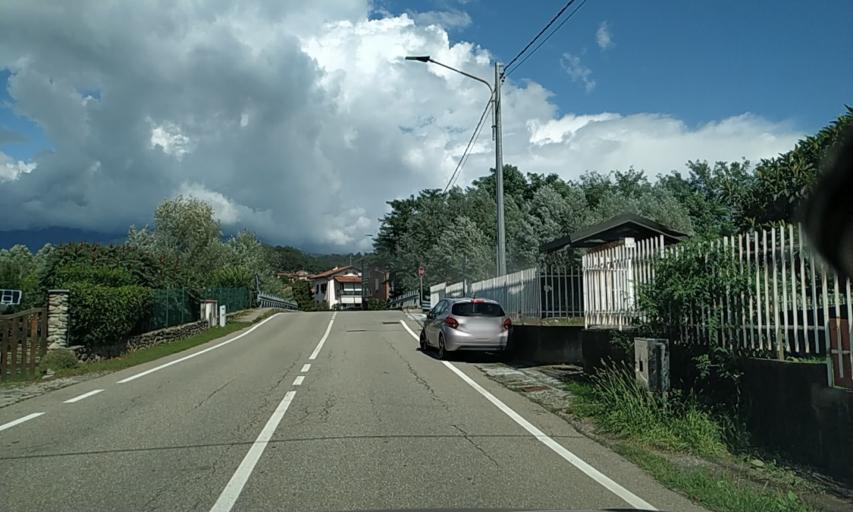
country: IT
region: Piedmont
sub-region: Provincia di Biella
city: Ceresane-Curanuova
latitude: 45.5222
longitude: 8.0065
